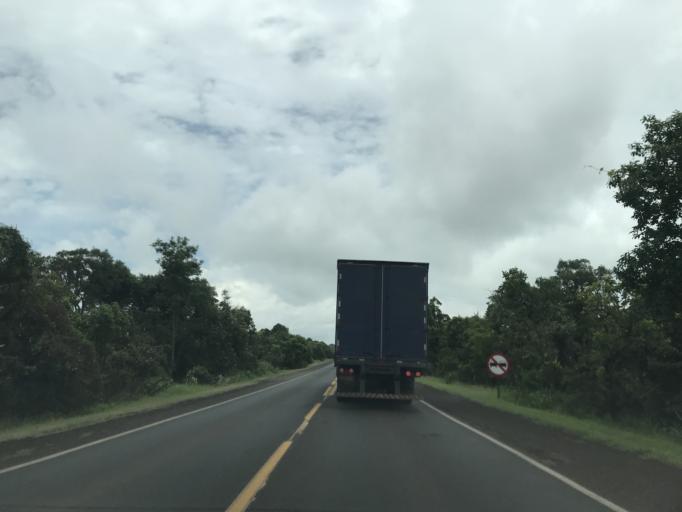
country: BR
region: Minas Gerais
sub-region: Frutal
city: Frutal
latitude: -19.7779
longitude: -48.9655
